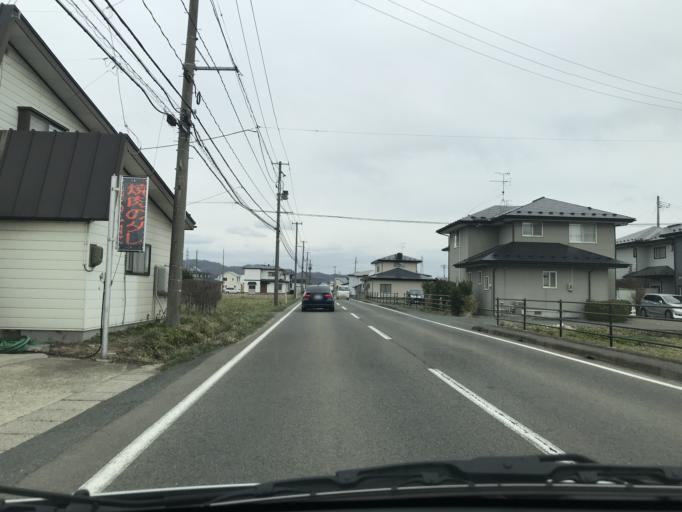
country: JP
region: Iwate
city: Kitakami
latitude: 39.2753
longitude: 141.0892
